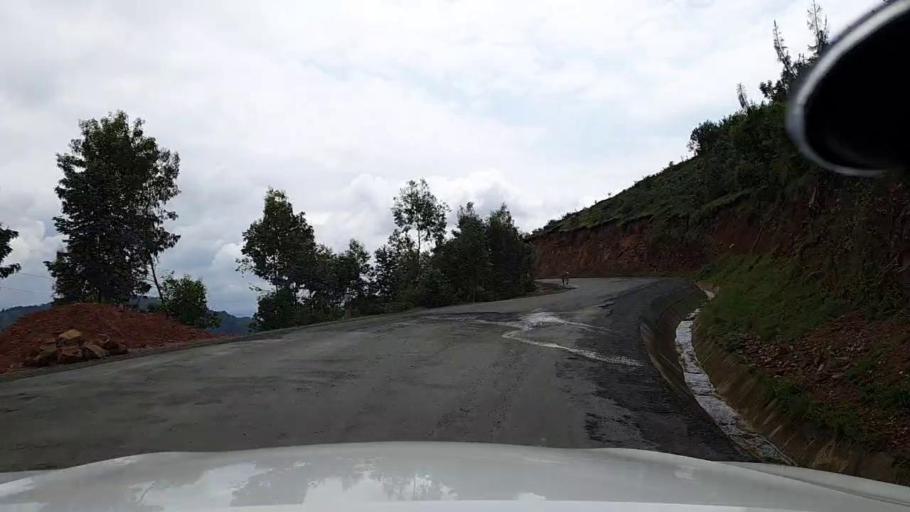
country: RW
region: Southern Province
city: Gitarama
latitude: -2.0683
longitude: 29.5614
